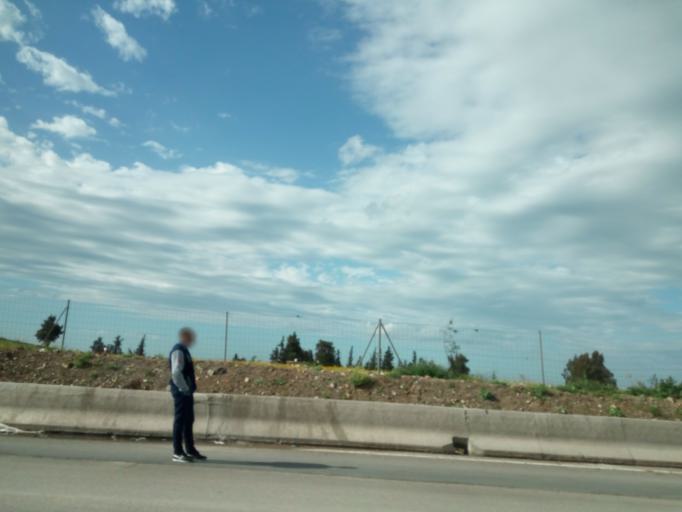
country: DZ
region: Tipaza
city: Mouzaia
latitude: 36.4483
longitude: 2.7120
